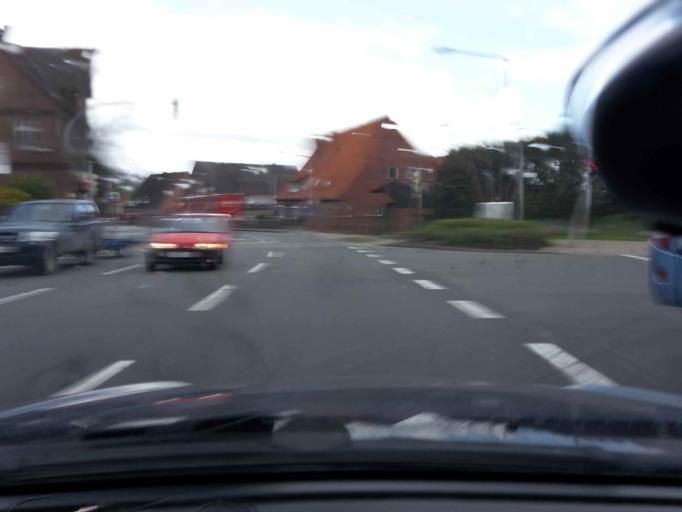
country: DE
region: Lower Saxony
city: Nottensdorf
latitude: 53.4806
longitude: 9.6363
